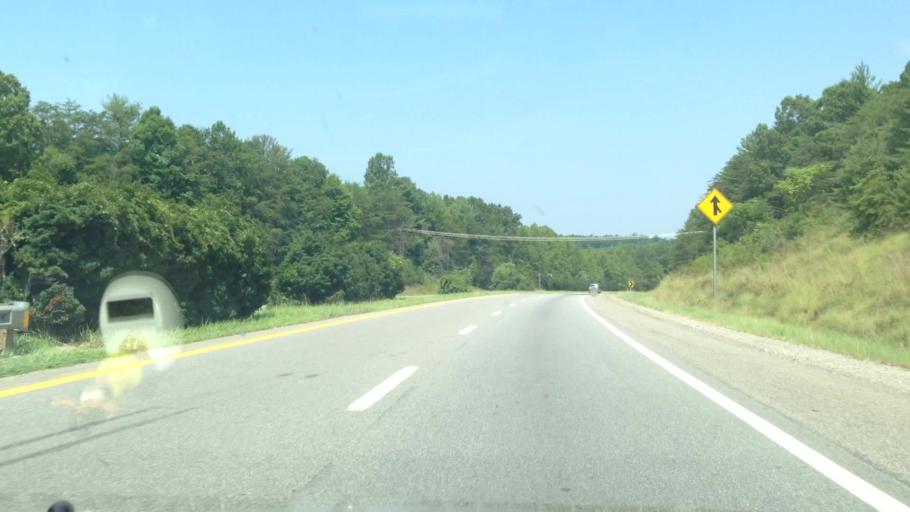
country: US
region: Virginia
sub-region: Henry County
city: Horse Pasture
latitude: 36.6491
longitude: -79.9163
